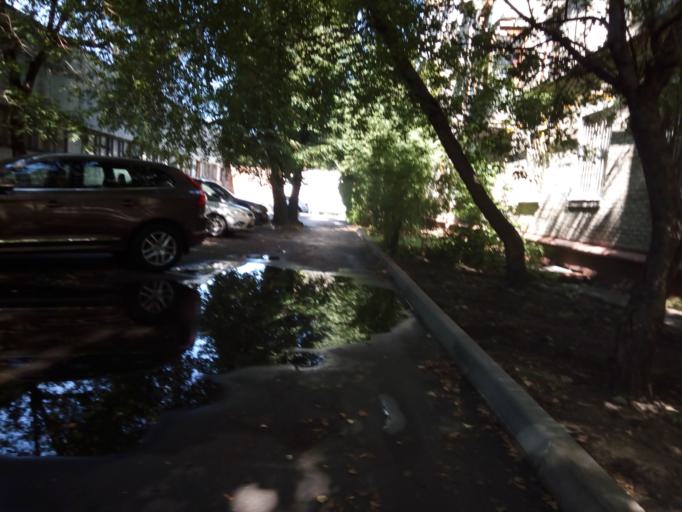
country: RU
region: Moskovskaya
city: Presnenskiy
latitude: 55.7728
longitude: 37.5340
